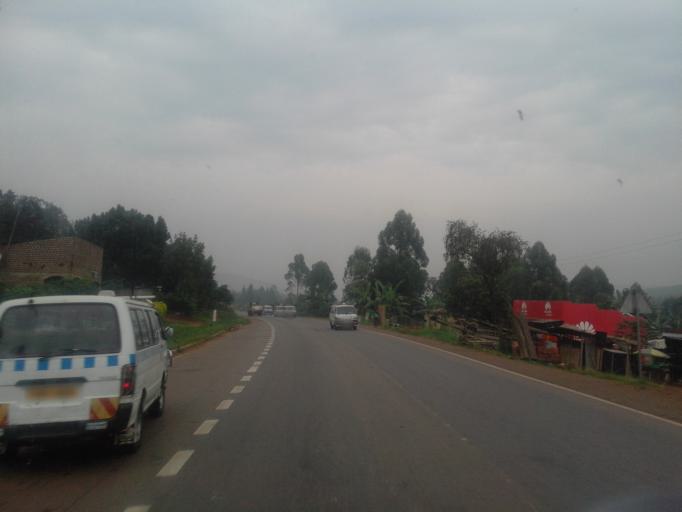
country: UG
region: Central Region
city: Lugazi
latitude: 0.3703
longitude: 32.8822
